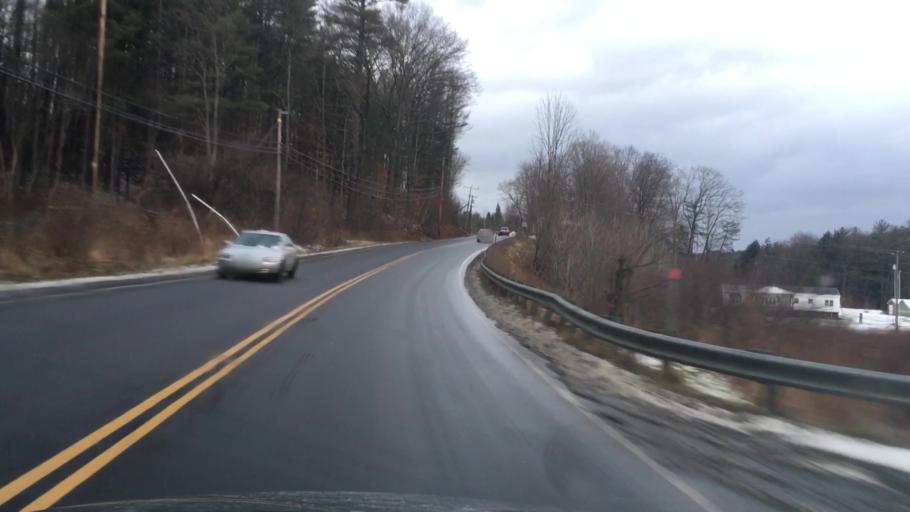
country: US
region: New Hampshire
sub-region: Sullivan County
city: Claremont
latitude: 43.3937
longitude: -72.3851
